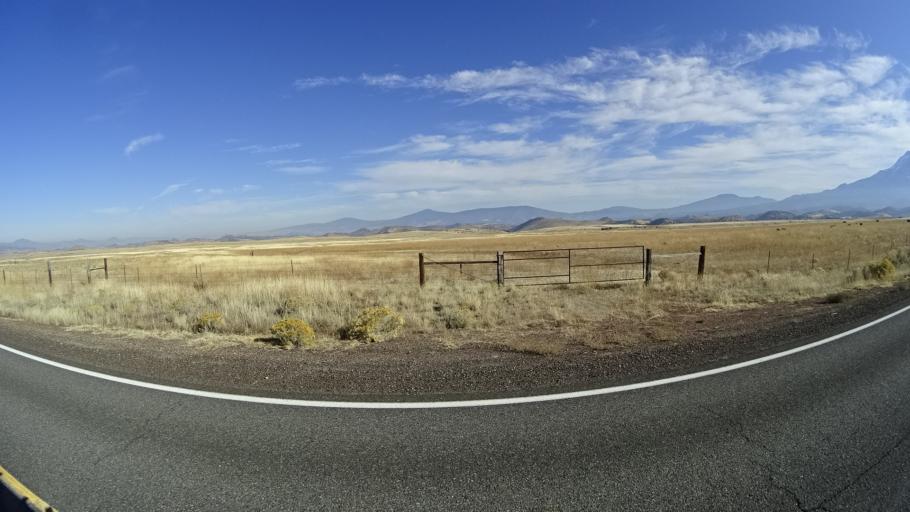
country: US
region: California
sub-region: Siskiyou County
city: Weed
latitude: 41.4795
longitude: -122.4931
